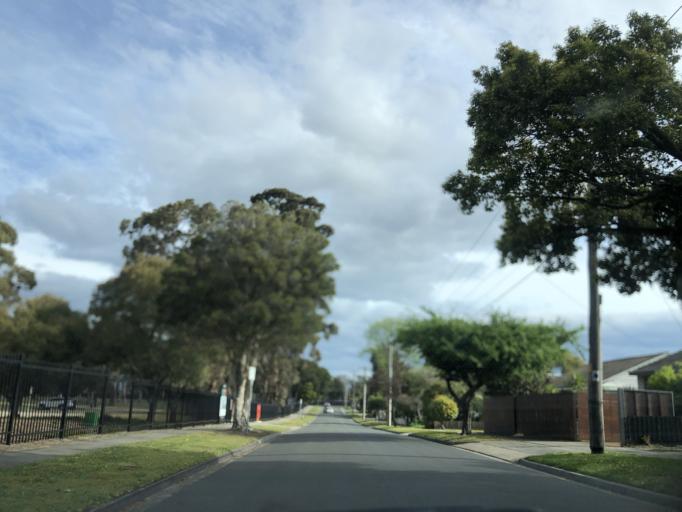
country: AU
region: Victoria
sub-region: Monash
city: Oakleigh South
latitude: -37.9227
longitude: 145.0896
